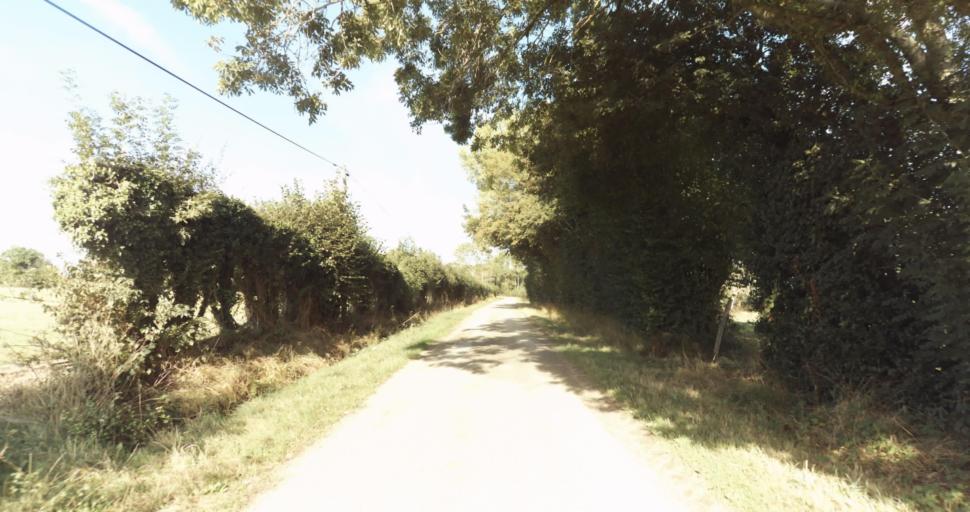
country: FR
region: Lower Normandy
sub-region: Departement du Calvados
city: La Vespiere
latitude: 48.9216
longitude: 0.3344
